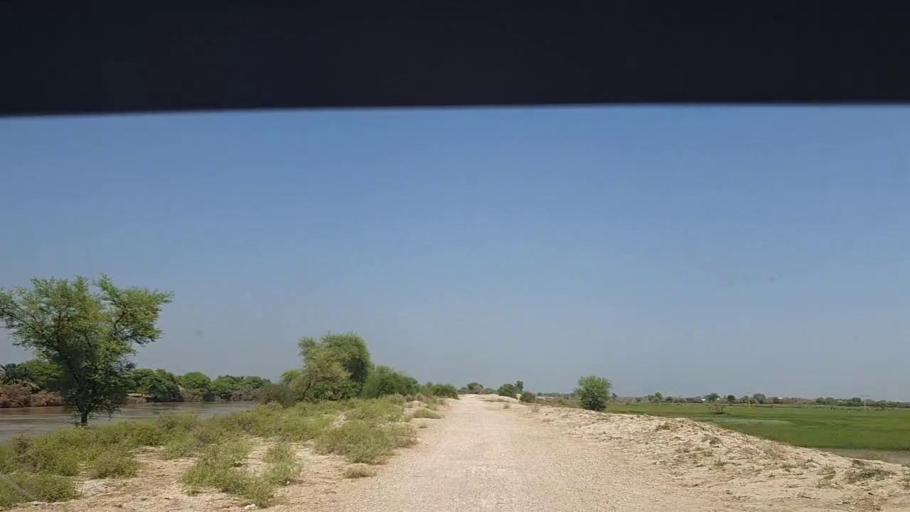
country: PK
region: Sindh
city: Kandhkot
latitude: 28.1905
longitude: 69.1636
